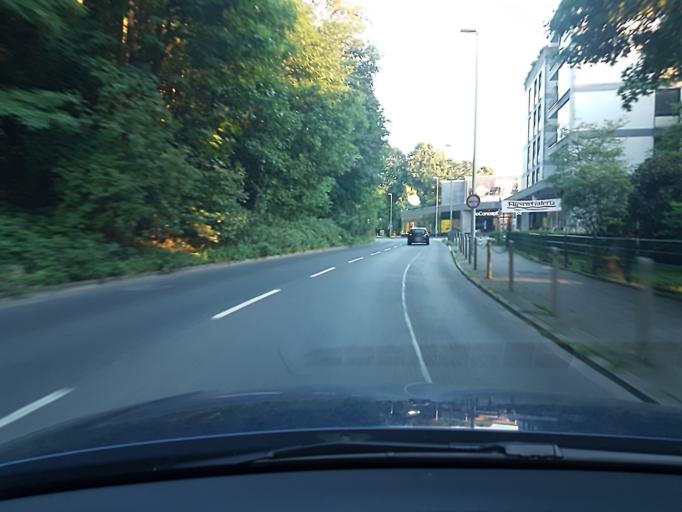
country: DE
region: North Rhine-Westphalia
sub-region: Regierungsbezirk Dusseldorf
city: Erkrath
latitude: 51.2167
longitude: 6.8664
